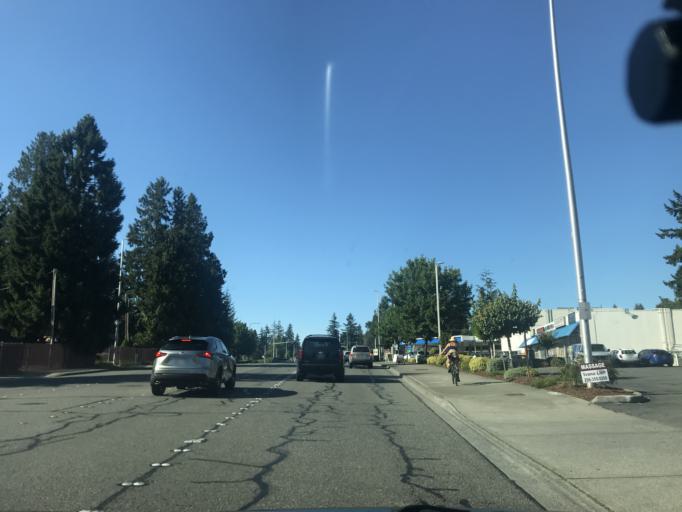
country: US
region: Washington
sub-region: King County
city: Lea Hill
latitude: 47.3653
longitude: -122.1867
